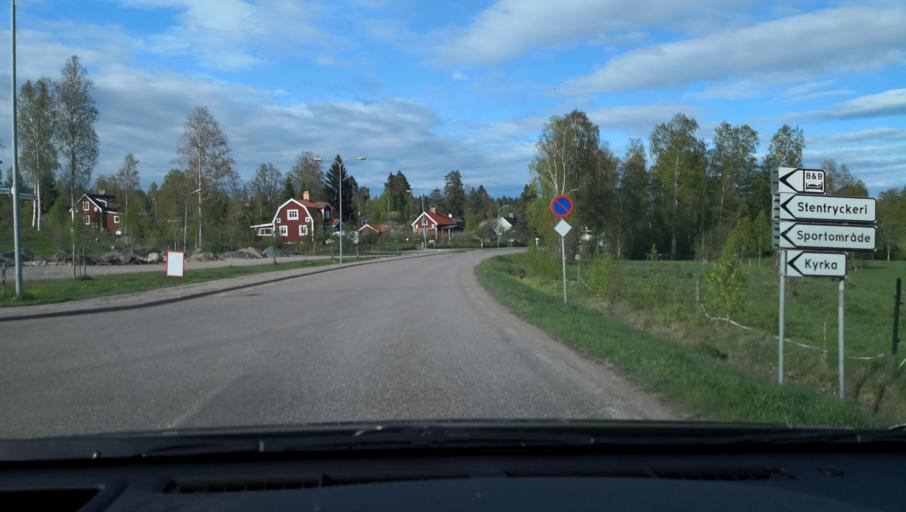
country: SE
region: Dalarna
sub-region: Saters Kommun
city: Saeter
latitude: 60.2977
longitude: 15.8269
